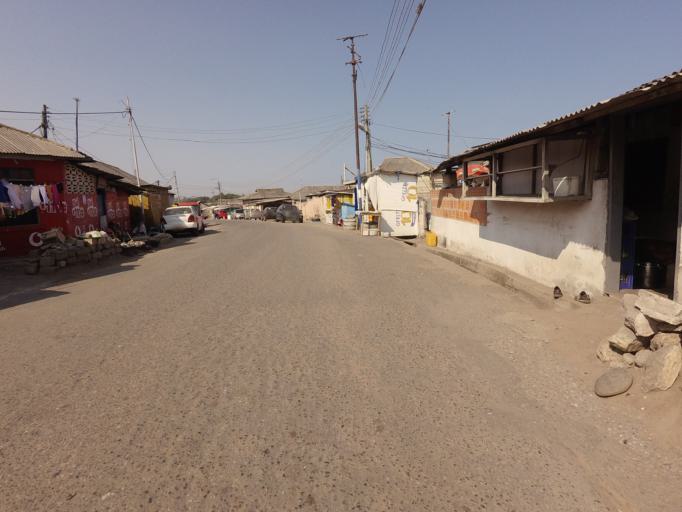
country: GH
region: Greater Accra
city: Teshi Old Town
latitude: 5.5798
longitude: -0.1015
